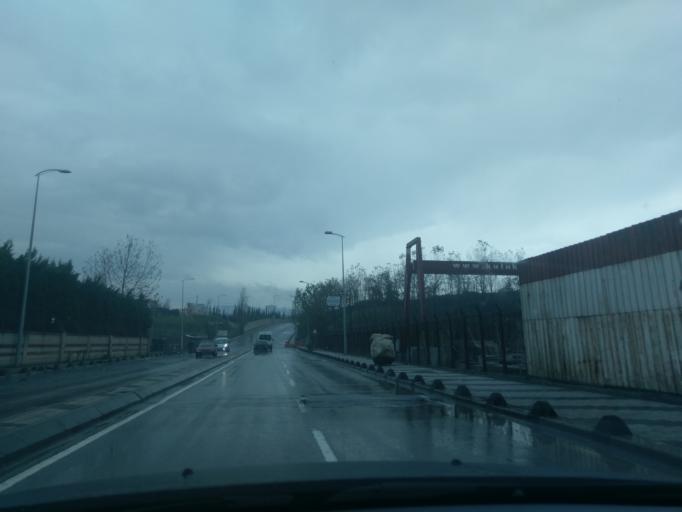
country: TR
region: Istanbul
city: Sancaktepe
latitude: 41.0251
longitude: 29.2373
